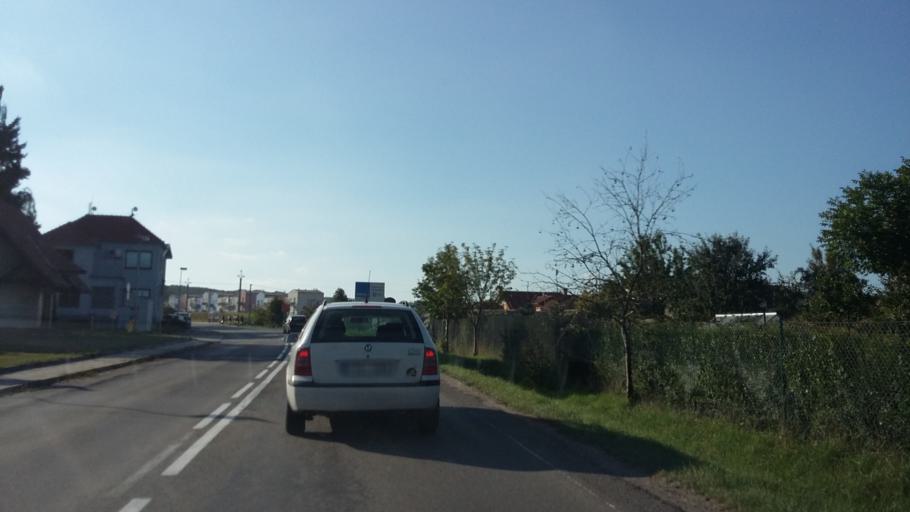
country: CZ
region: South Moravian
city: Troubsko
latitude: 49.1809
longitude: 16.4930
